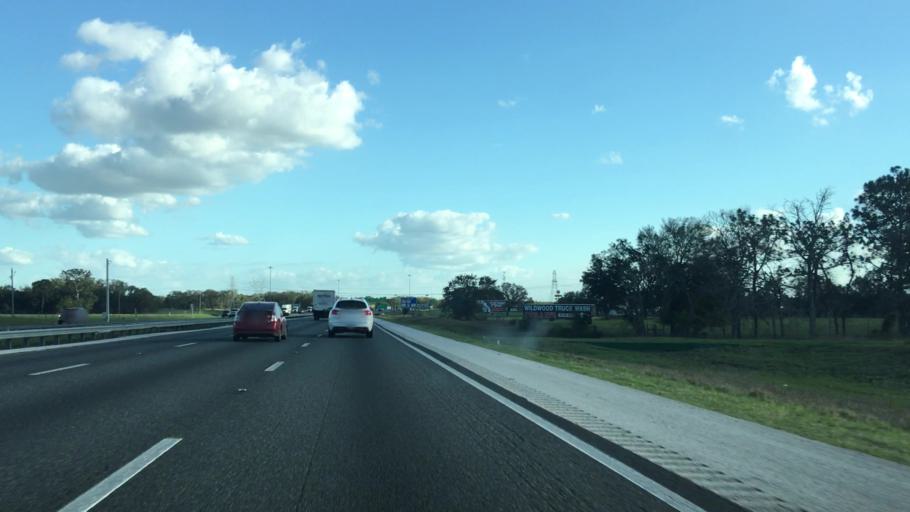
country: US
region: Florida
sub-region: Sumter County
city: Wildwood
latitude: 28.8882
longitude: -82.0969
